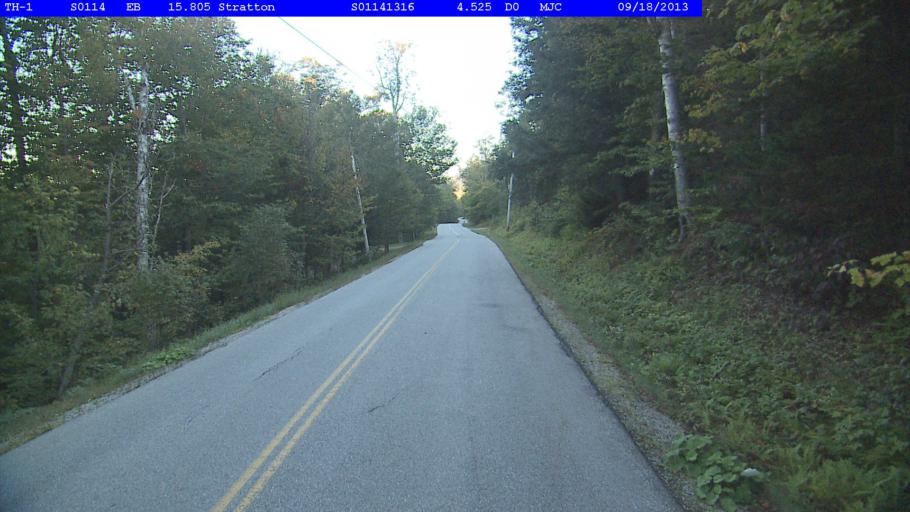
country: US
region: Vermont
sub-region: Windham County
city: Dover
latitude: 43.0485
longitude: -72.9216
